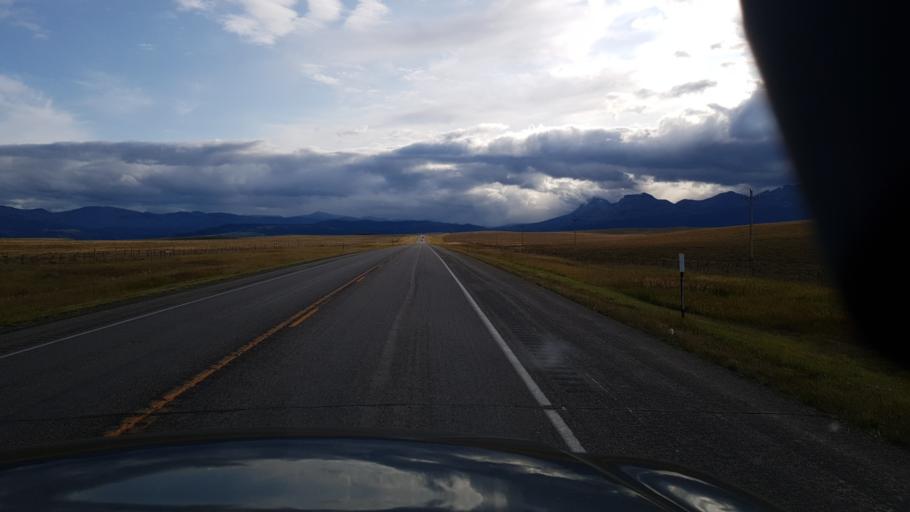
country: US
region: Montana
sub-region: Glacier County
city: South Browning
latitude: 48.4817
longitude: -113.1377
